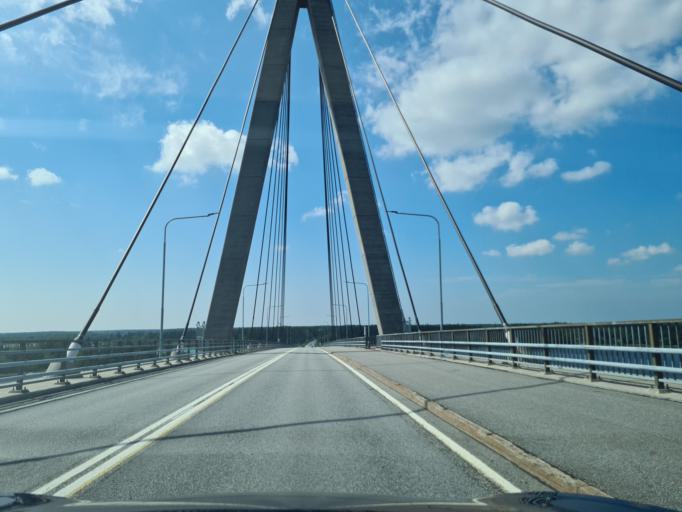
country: FI
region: Ostrobothnia
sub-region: Vaasa
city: Replot
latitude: 63.2072
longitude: 21.4701
